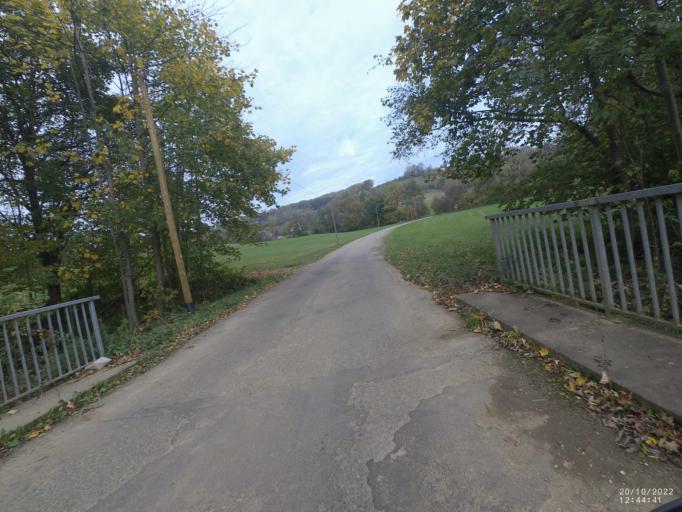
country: DE
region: Baden-Wuerttemberg
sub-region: Regierungsbezirk Stuttgart
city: Ottenbach
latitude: 48.7247
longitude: 9.7885
